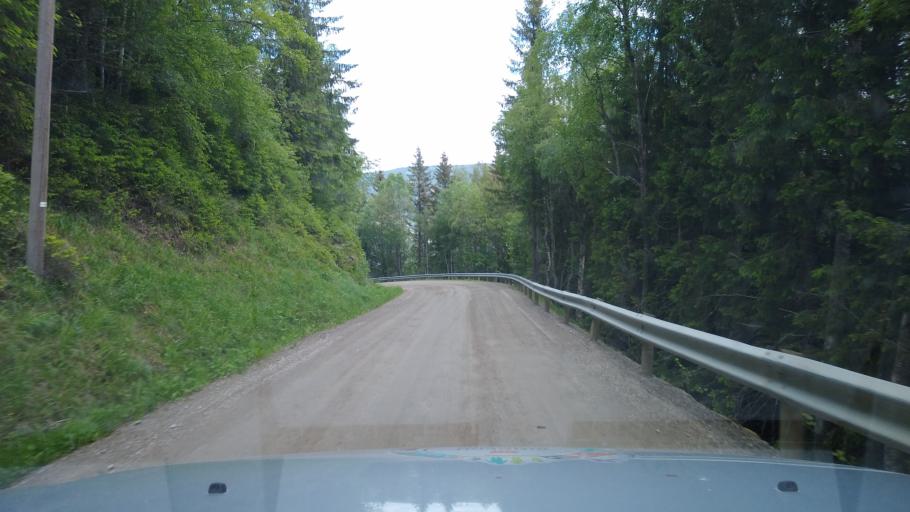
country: NO
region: Oppland
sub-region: Ringebu
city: Ringebu
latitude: 61.5056
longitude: 10.1376
